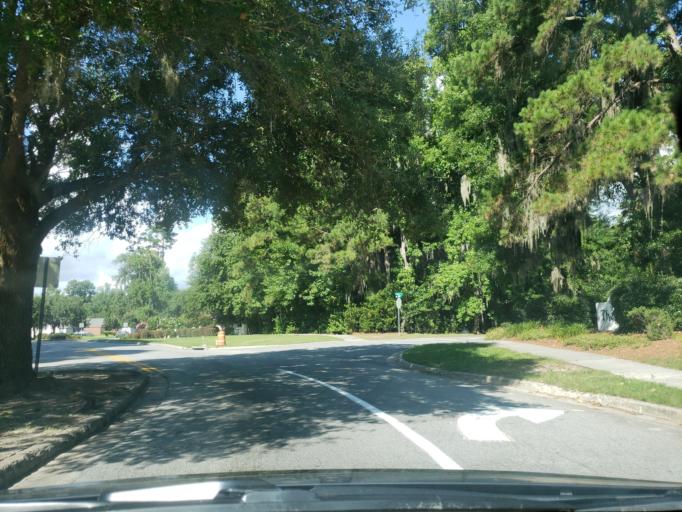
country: US
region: Georgia
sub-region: Chatham County
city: Georgetown
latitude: 31.9802
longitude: -81.2271
